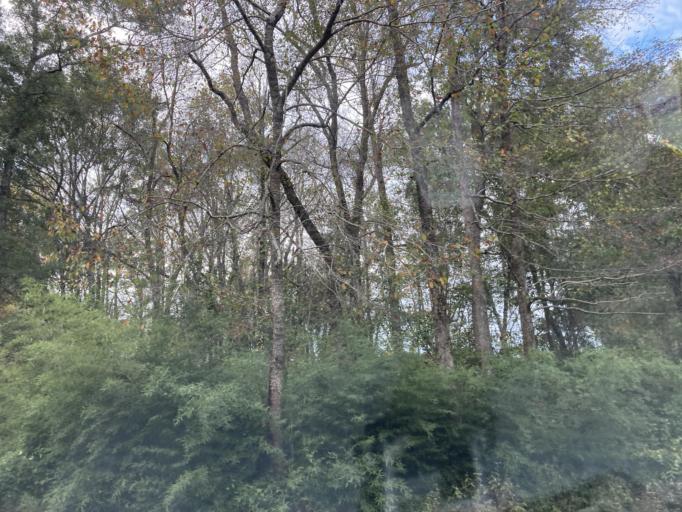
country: US
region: Mississippi
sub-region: Lamar County
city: West Hattiesburg
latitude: 31.3245
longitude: -89.4679
